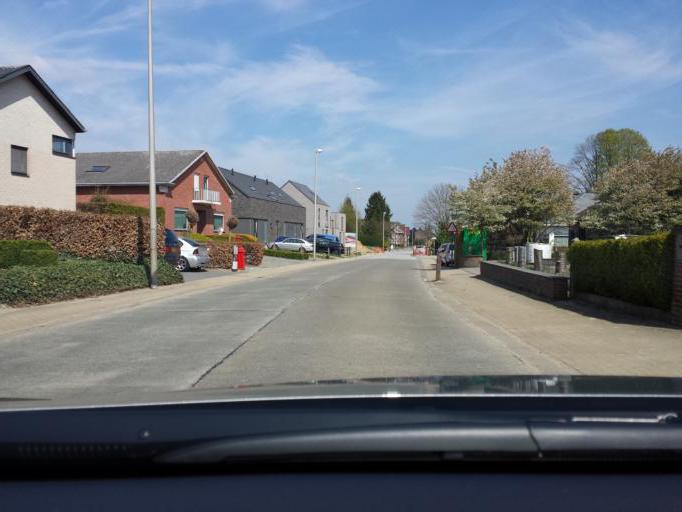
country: BE
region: Flanders
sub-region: Provincie Vlaams-Brabant
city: Kortenberg
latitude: 50.9006
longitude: 4.5480
